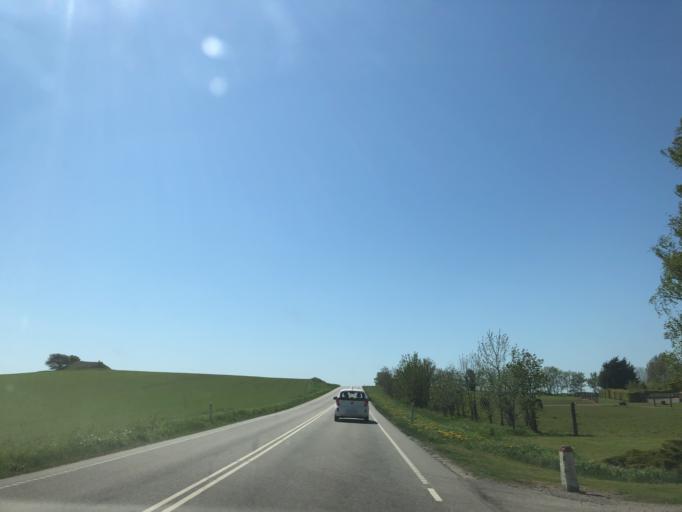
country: DK
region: Zealand
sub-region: Slagelse Kommune
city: Forlev
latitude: 55.3485
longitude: 11.2341
